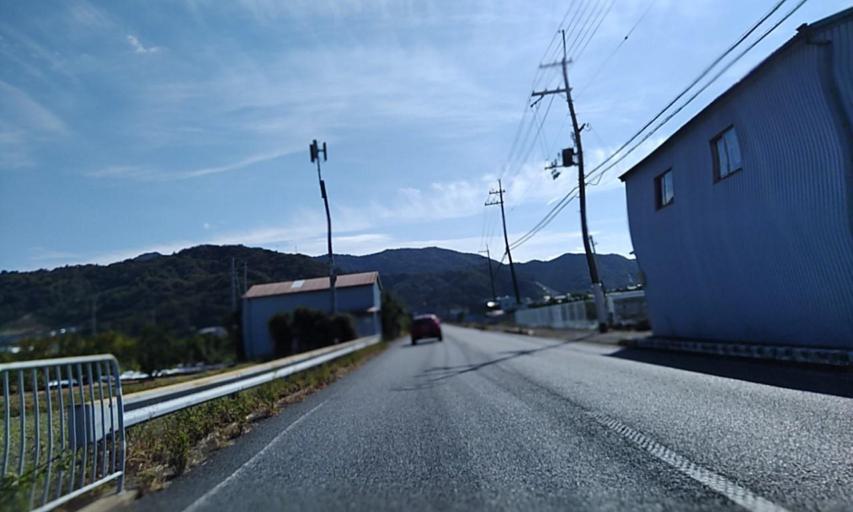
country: JP
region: Wakayama
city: Kainan
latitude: 34.0183
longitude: 135.1830
